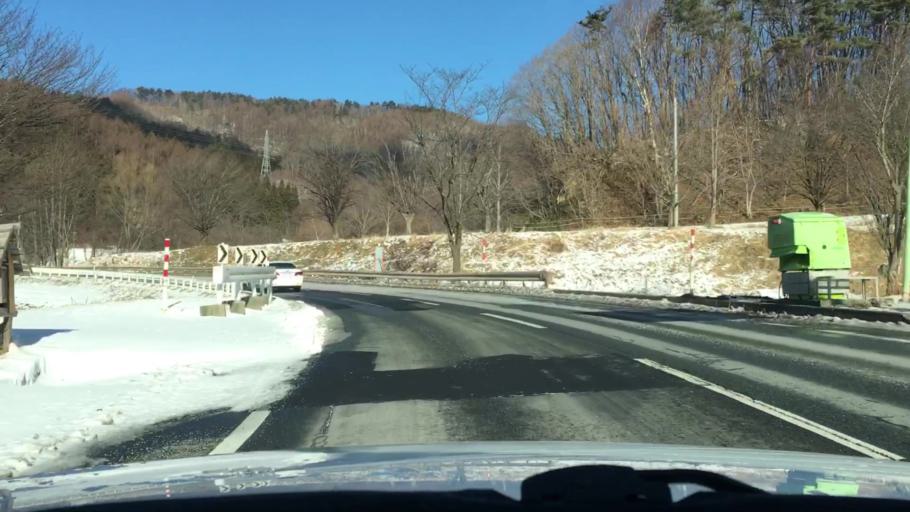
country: JP
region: Iwate
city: Morioka-shi
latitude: 39.6702
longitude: 141.3302
